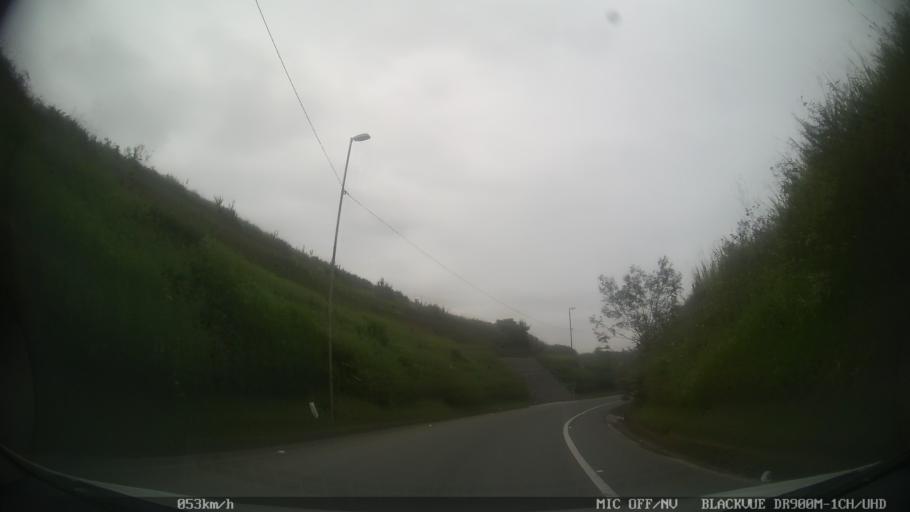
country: BR
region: Santa Catarina
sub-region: Joinville
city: Joinville
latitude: -26.3863
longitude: -48.8470
